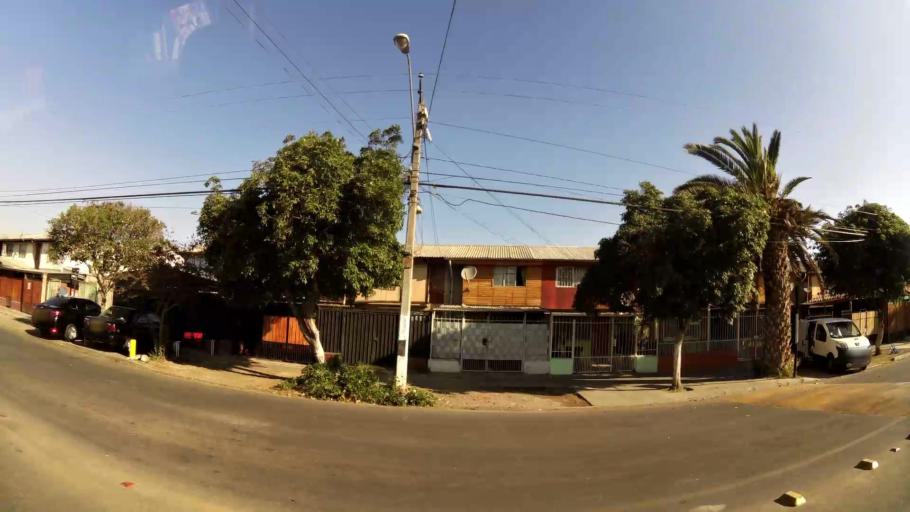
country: CL
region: Santiago Metropolitan
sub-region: Provincia de Santiago
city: La Pintana
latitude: -33.5469
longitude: -70.6266
